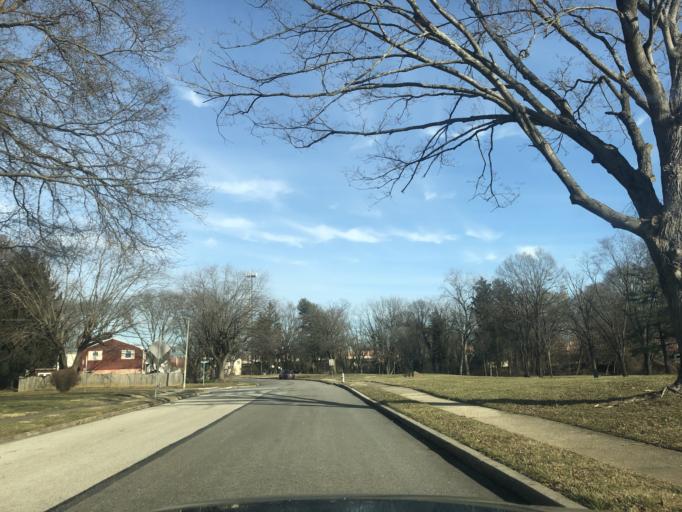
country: US
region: Pennsylvania
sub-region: Montgomery County
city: Flourtown
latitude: 40.1120
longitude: -75.2043
